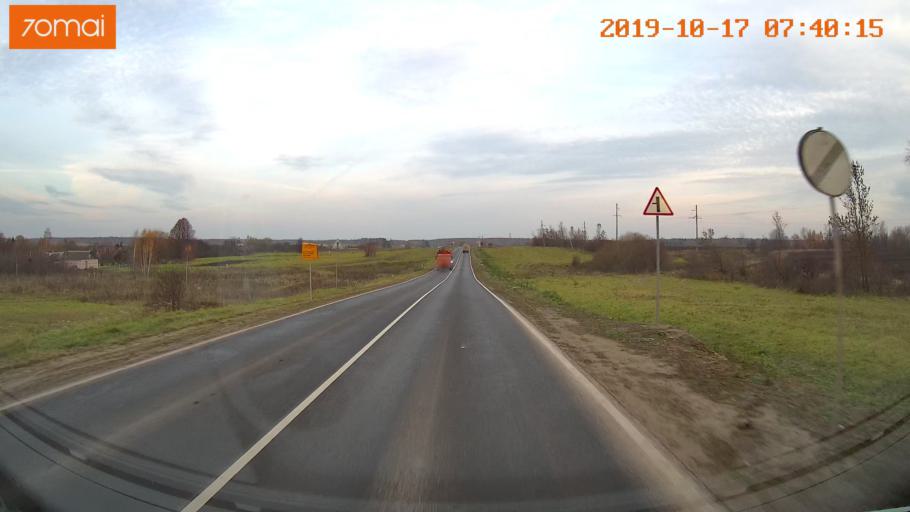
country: RU
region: Vladimir
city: Yur'yev-Pol'skiy
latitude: 56.4707
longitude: 39.8337
